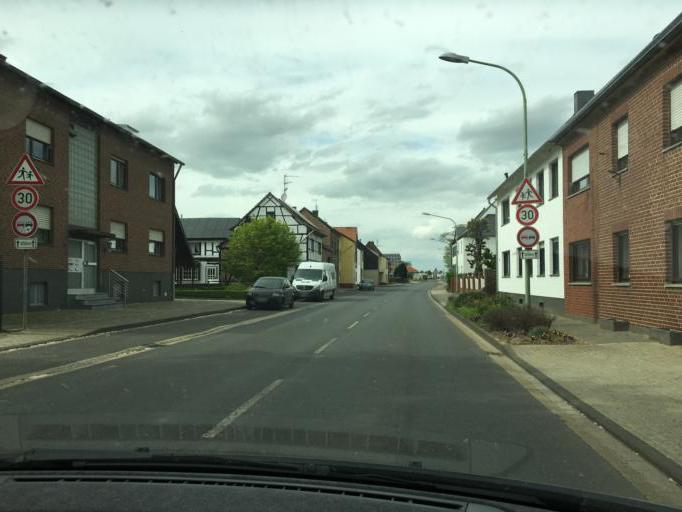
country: DE
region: North Rhine-Westphalia
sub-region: Regierungsbezirk Koln
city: Vettweiss
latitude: 50.7696
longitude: 6.5946
